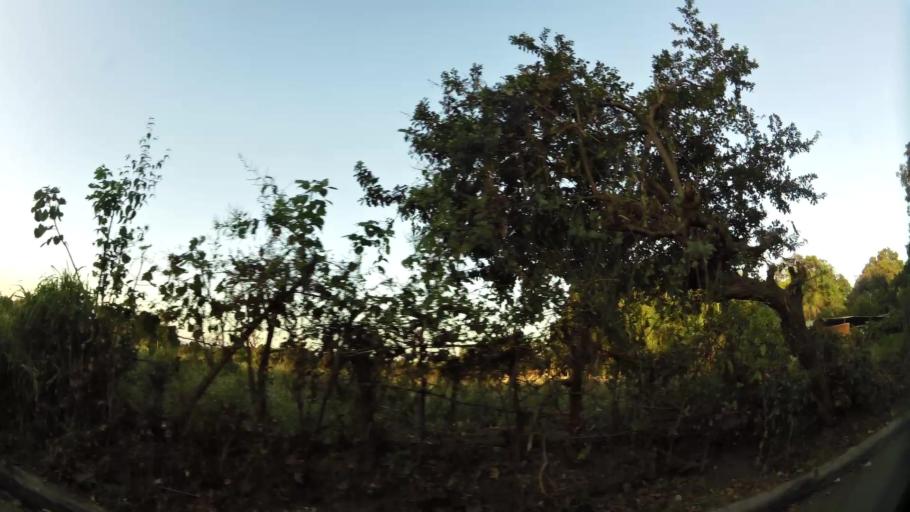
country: SV
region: Sonsonate
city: Armenia
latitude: 13.7394
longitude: -89.3904
